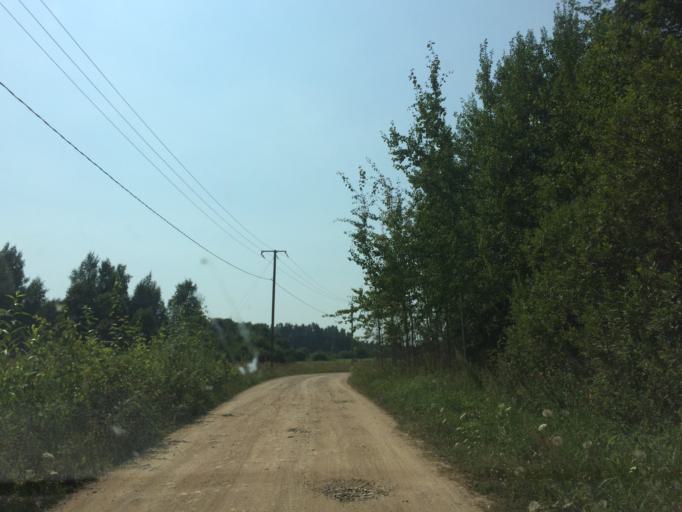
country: LV
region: Ludzas Rajons
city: Ludza
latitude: 56.5441
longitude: 27.5859
